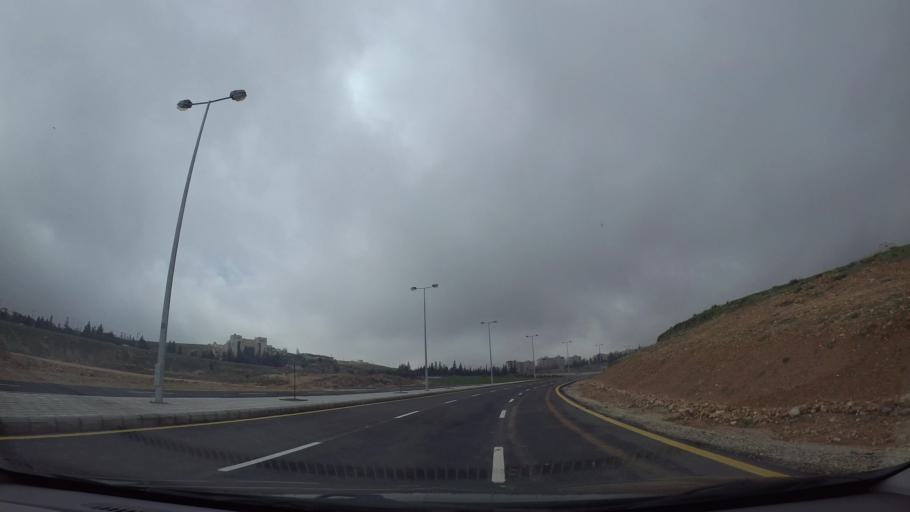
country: JO
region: Amman
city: Wadi as Sir
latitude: 31.9337
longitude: 35.8595
